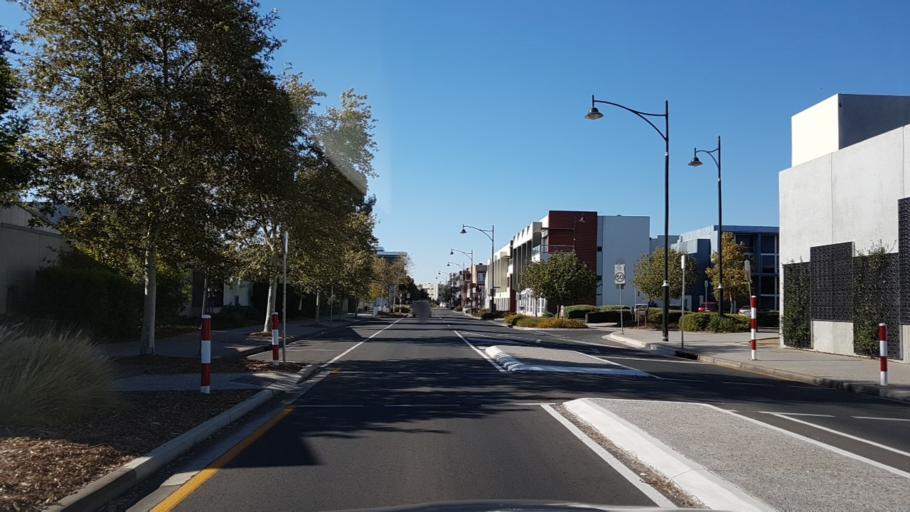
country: AU
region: South Australia
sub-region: Salisbury
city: Ingle Farm
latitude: -34.8096
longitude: 138.6148
